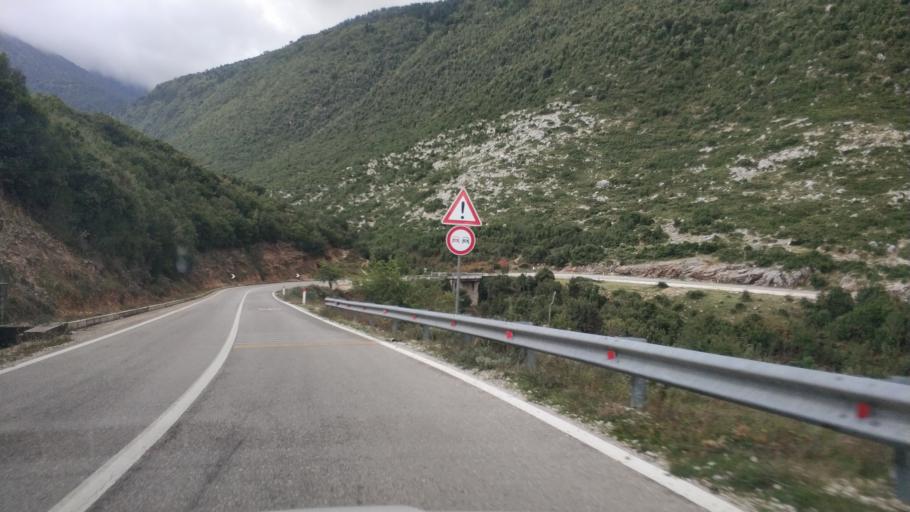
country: AL
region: Vlore
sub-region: Rrethi i Vlores
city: Brataj
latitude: 40.2339
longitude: 19.5592
